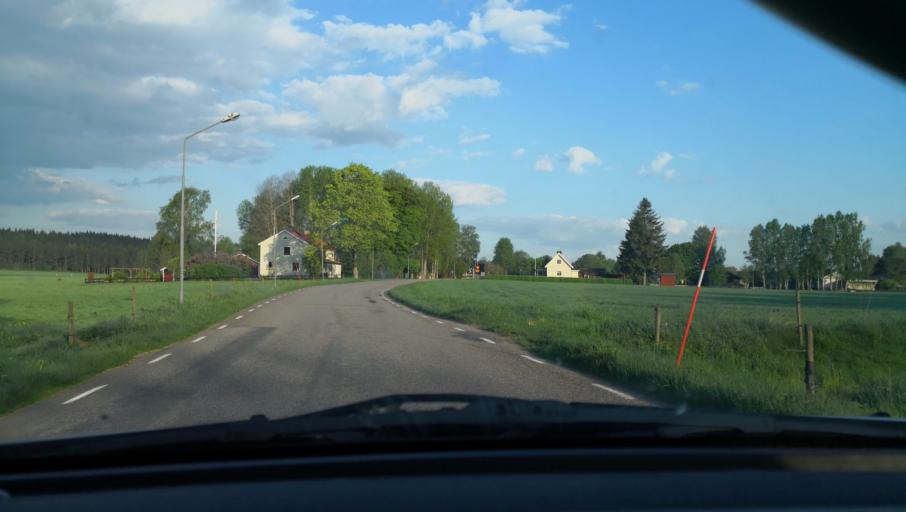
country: SE
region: Joenkoeping
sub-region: Nassjo Kommun
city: Bodafors
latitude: 57.4658
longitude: 14.7628
